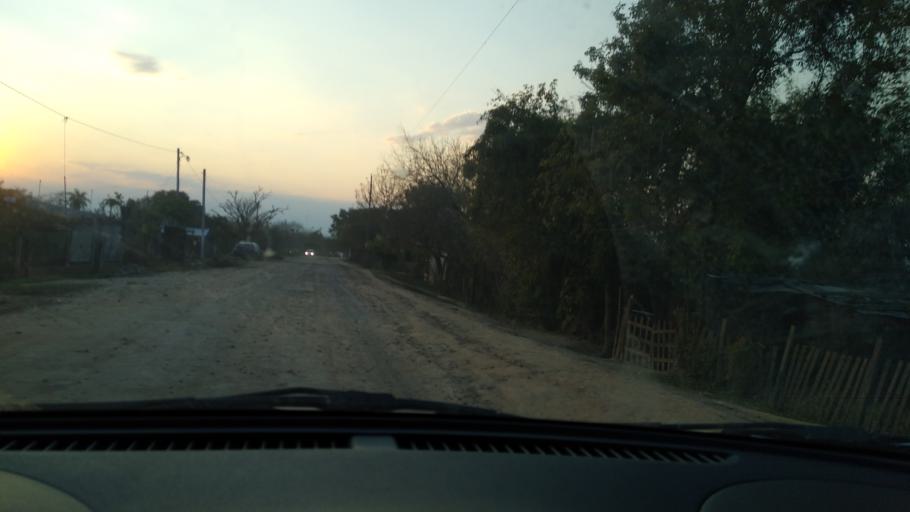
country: AR
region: Chaco
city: Barranqueras
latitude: -27.4624
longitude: -58.9553
